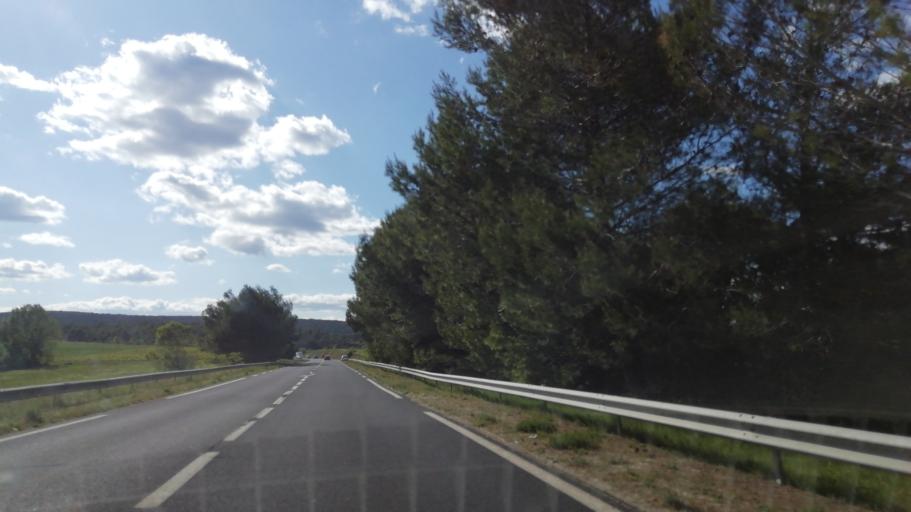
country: FR
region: Languedoc-Roussillon
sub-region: Departement de l'Herault
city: Saint-Gely-du-Fesc
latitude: 43.7078
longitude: 3.8103
